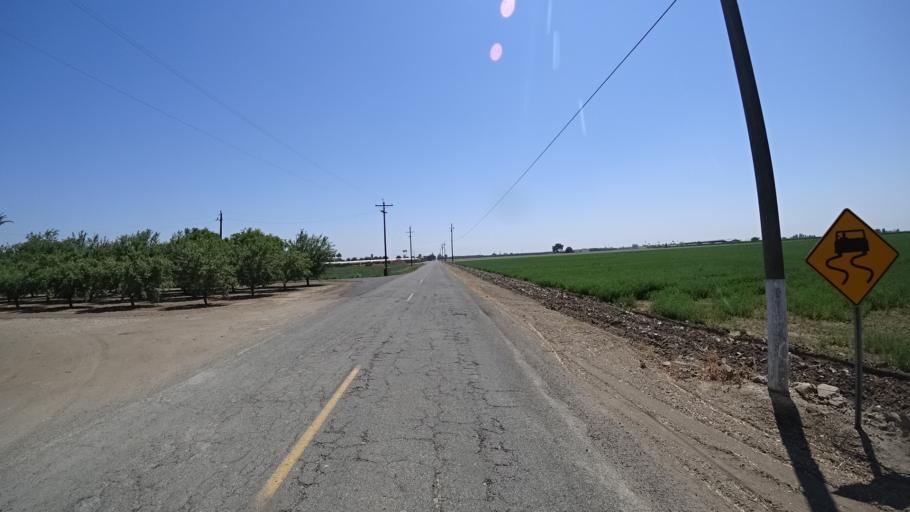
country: US
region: California
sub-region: Kings County
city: Armona
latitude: 36.3572
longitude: -119.7343
